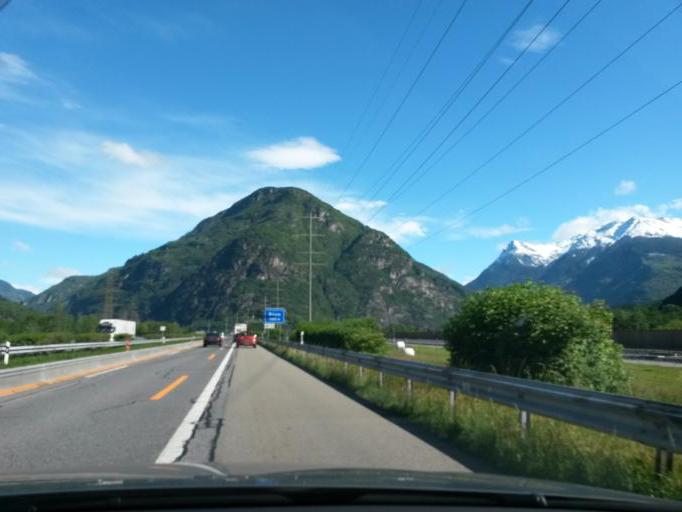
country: CH
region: Ticino
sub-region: Riviera District
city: Biasca
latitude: 46.3432
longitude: 8.9683
